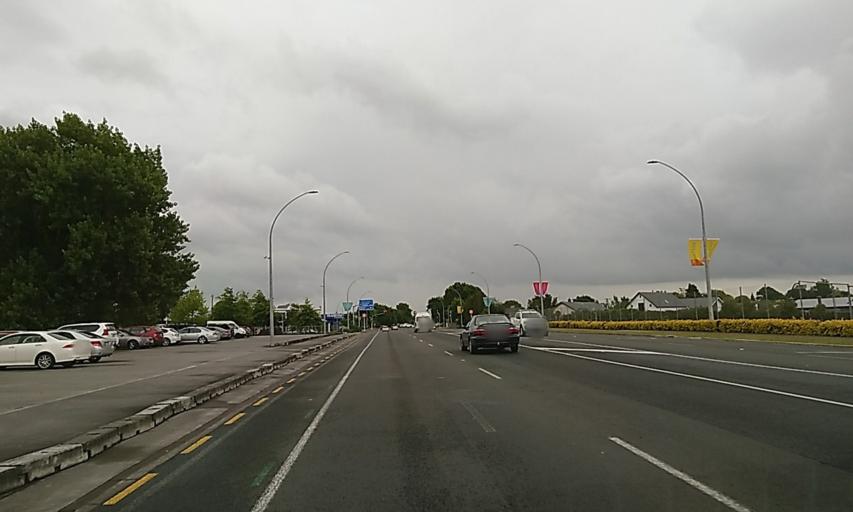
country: NZ
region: Waikato
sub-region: Hamilton City
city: Hamilton
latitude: -37.7829
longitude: 175.2692
